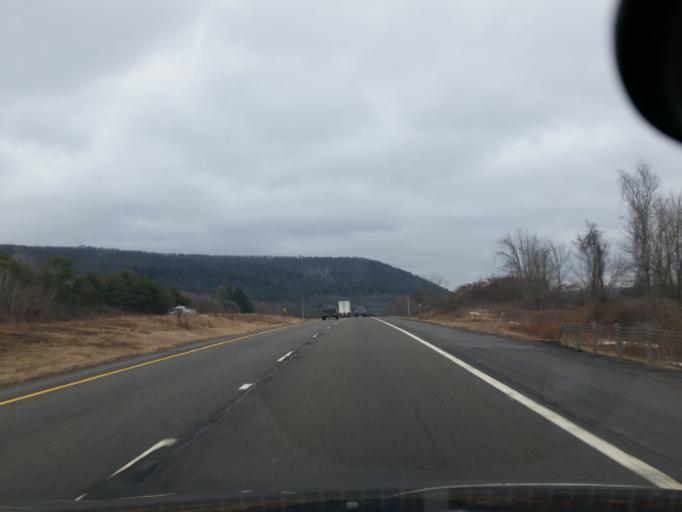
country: US
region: New York
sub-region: Broome County
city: Chenango Bridge
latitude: 42.0700
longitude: -75.8002
